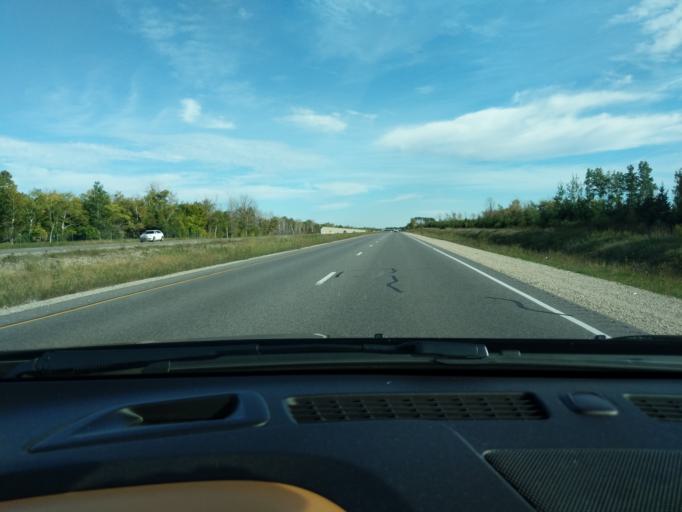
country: CA
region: Ontario
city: Collingwood
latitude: 44.4796
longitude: -80.1644
